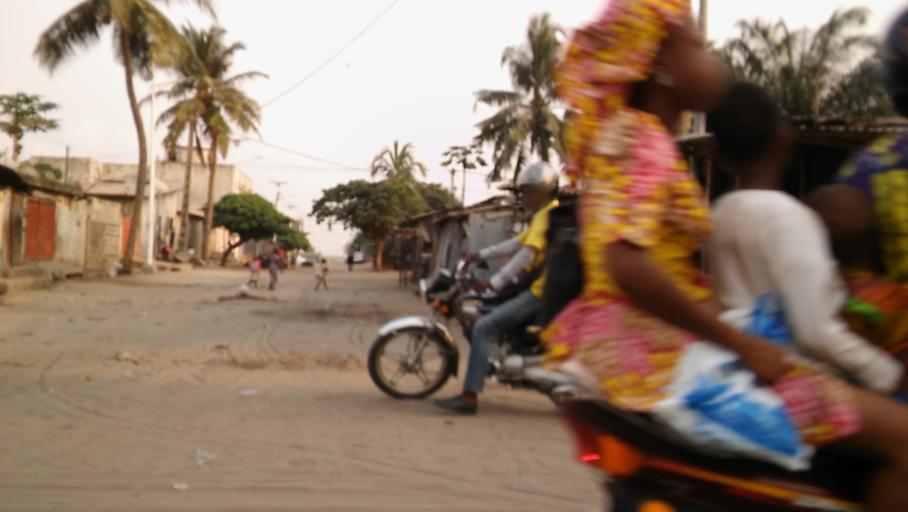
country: BJ
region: Littoral
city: Cotonou
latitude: 6.3929
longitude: 2.3809
